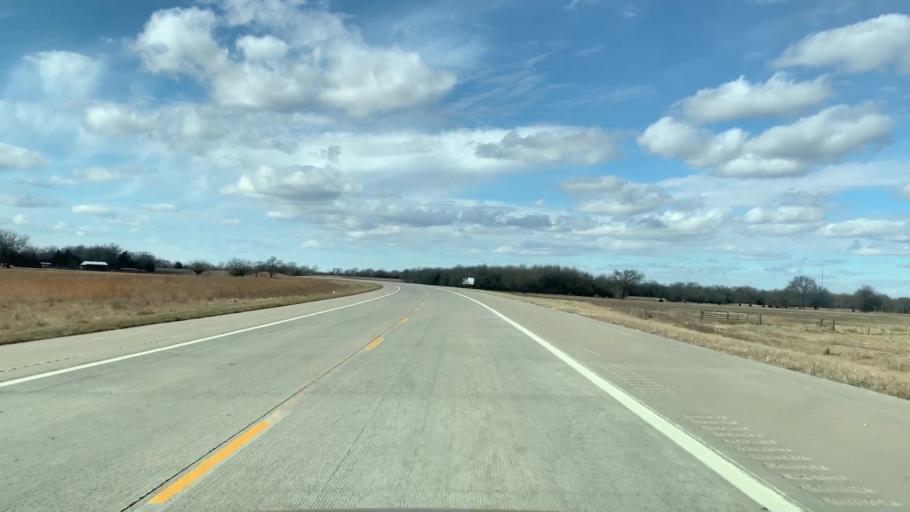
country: US
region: Kansas
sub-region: Labette County
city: Parsons
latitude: 37.3574
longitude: -95.2170
